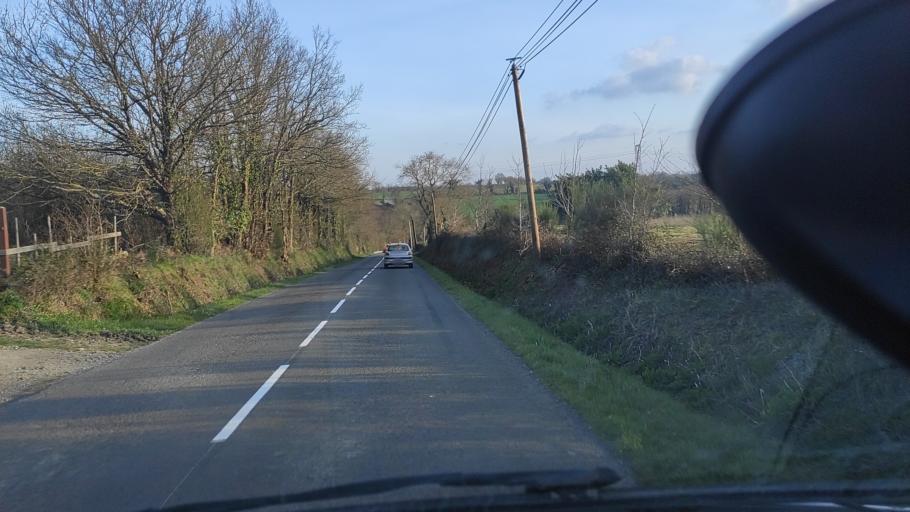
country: FR
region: Pays de la Loire
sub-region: Departement de la Vendee
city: La Chaize-le-Vicomte
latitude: 46.6554
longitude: -1.2987
